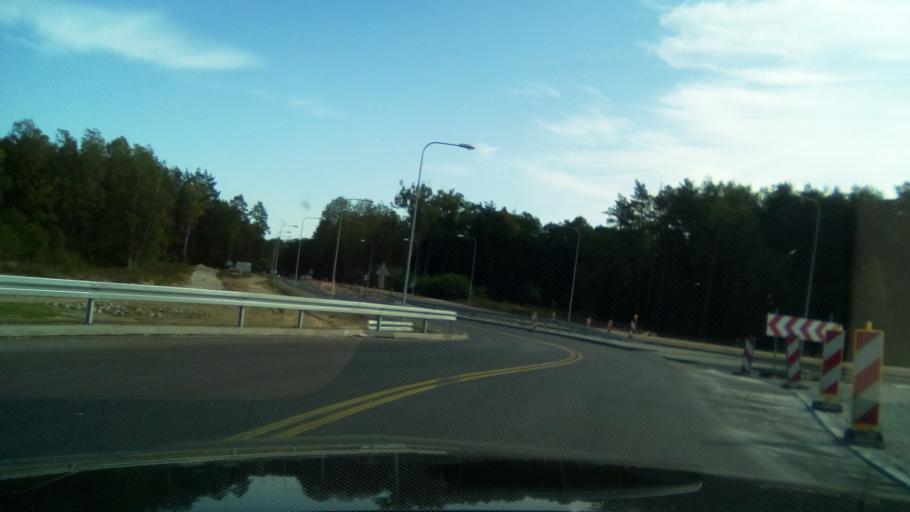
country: PL
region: West Pomeranian Voivodeship
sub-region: Powiat walecki
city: Walcz
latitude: 53.2862
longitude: 16.5077
